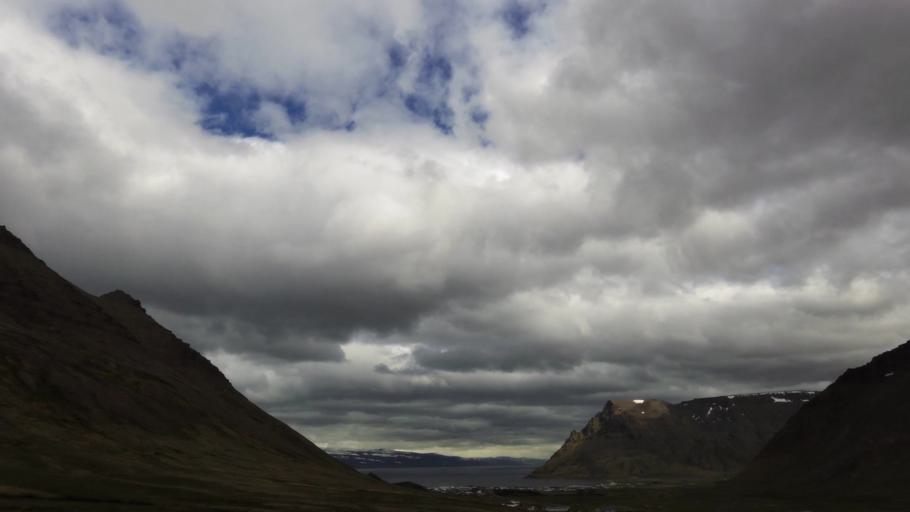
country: IS
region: Westfjords
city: Isafjoerdur
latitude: 66.1615
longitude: -23.3053
